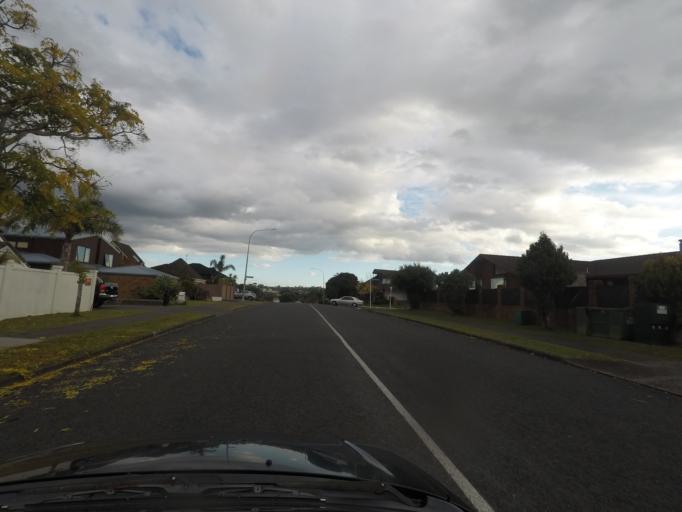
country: NZ
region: Auckland
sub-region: Auckland
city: Rosebank
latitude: -36.8049
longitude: 174.6429
